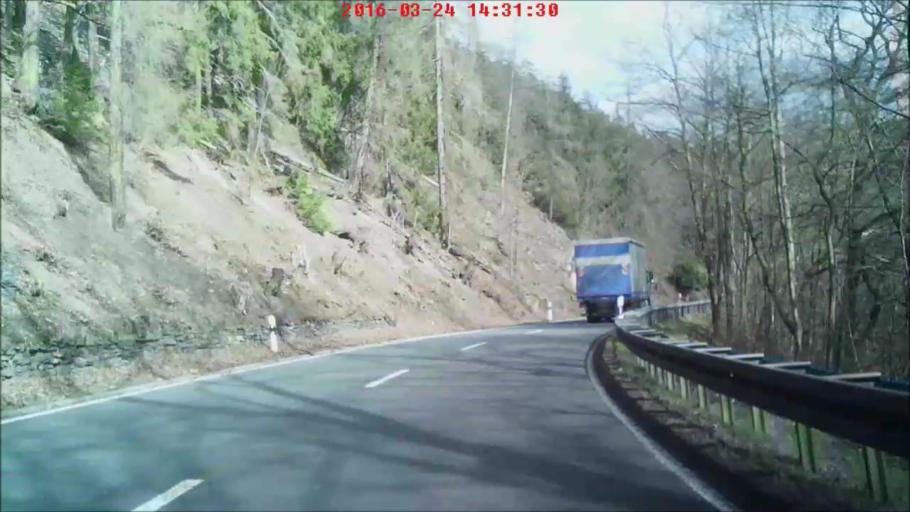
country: DE
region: Thuringia
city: Schwarzburg
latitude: 50.6482
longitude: 11.1889
